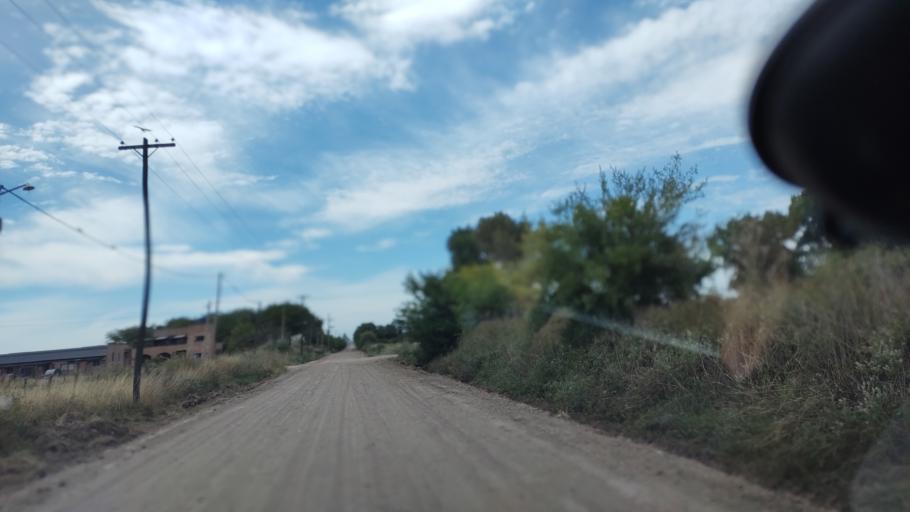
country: AR
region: Buenos Aires
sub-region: Partido de Lobos
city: Lobos
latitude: -35.1644
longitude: -59.1089
